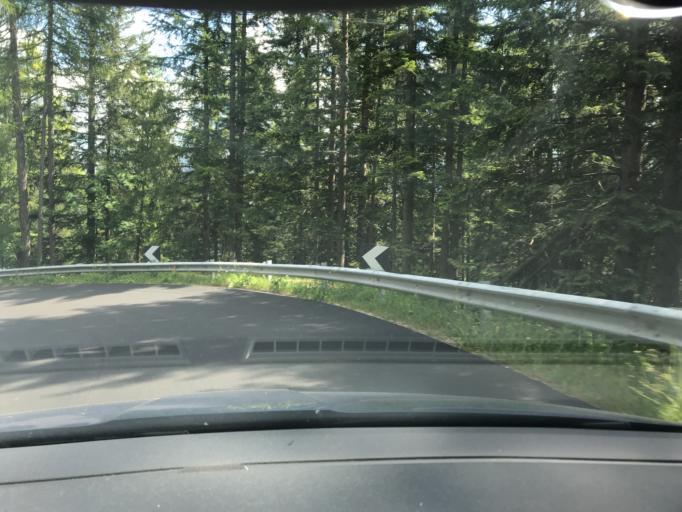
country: IT
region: Veneto
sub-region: Provincia di Belluno
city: Cortina d'Ampezzo
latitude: 46.5215
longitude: 12.1038
